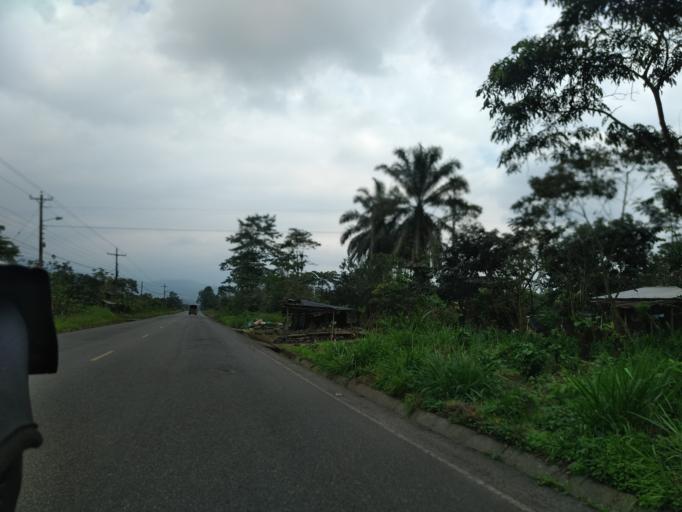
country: EC
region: Cotopaxi
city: La Mana
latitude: -0.8833
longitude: -79.1609
